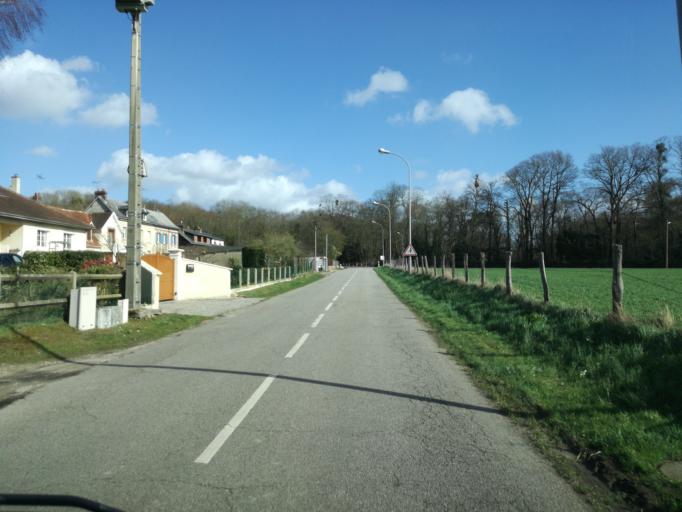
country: FR
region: Haute-Normandie
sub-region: Departement de la Seine-Maritime
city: Sahurs
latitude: 49.3569
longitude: 0.9555
